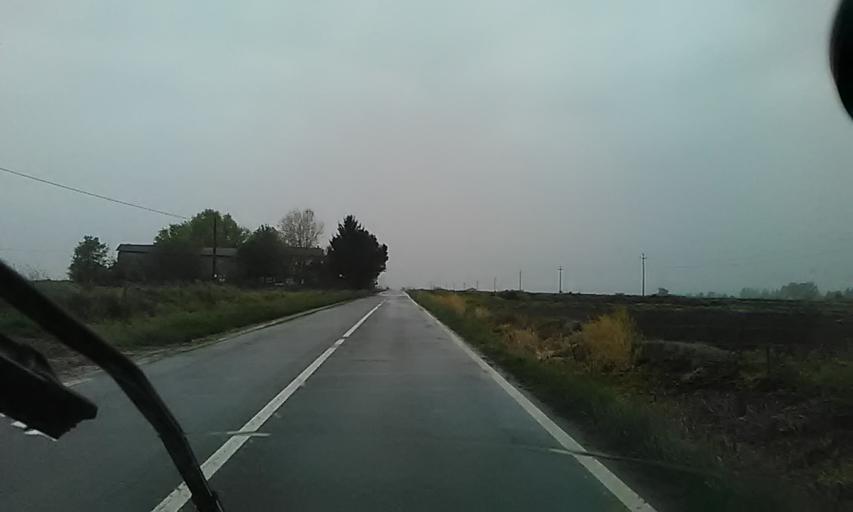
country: IT
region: Piedmont
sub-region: Provincia di Vercelli
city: Arborio
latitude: 45.4970
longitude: 8.3698
